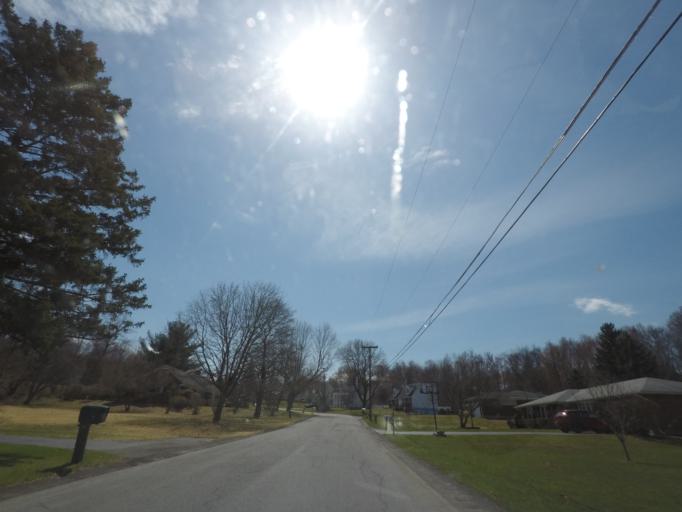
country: US
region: New York
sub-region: Rensselaer County
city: Wynantskill
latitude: 42.6966
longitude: -73.6624
